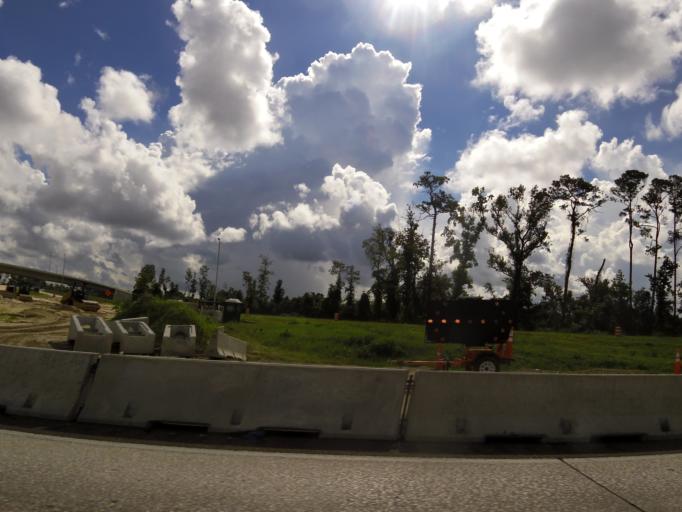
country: US
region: Florida
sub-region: Duval County
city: Jacksonville
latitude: 30.4578
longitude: -81.6496
